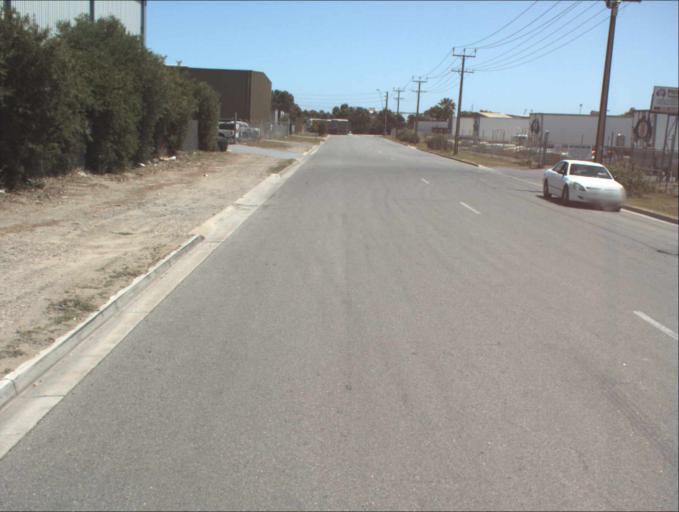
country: AU
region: South Australia
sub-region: Port Adelaide Enfield
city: Alberton
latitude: -34.8363
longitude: 138.5325
